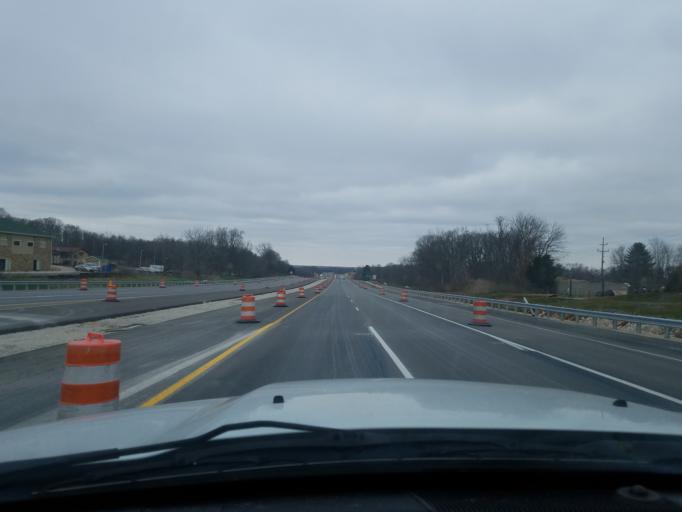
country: US
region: Indiana
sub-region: Monroe County
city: Bloomington
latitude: 39.1951
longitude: -86.5545
